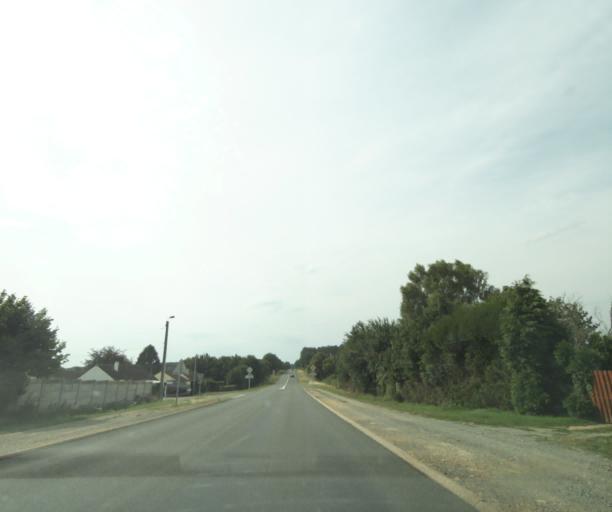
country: FR
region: Pays de la Loire
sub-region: Departement de la Sarthe
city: Marigne-Laille
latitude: 47.7936
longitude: 0.3363
